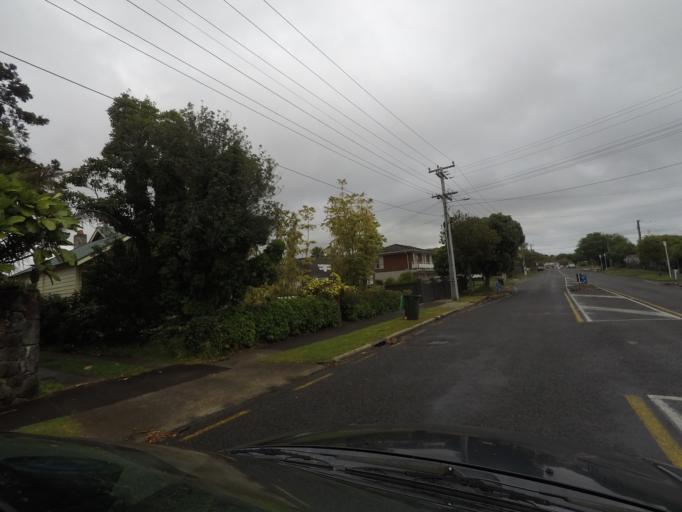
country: NZ
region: Auckland
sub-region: Auckland
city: Auckland
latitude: -36.8868
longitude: 174.7330
